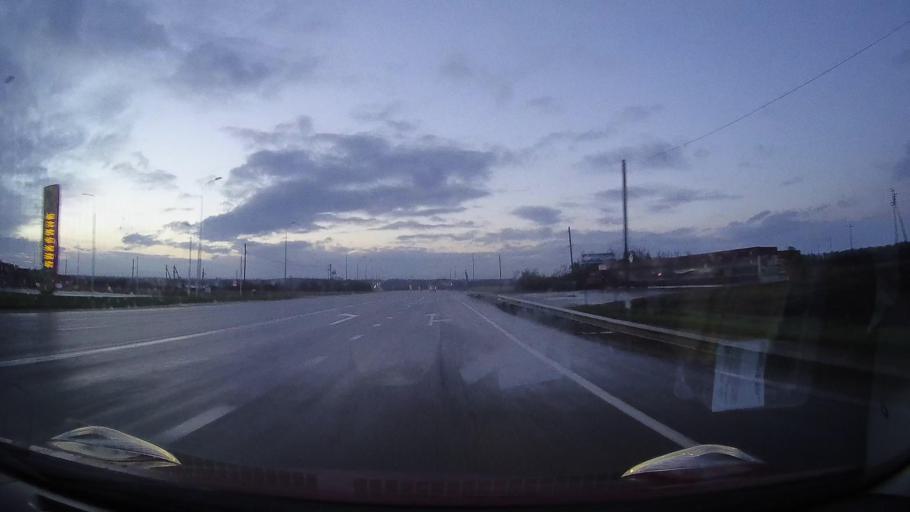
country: RU
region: Krasnodarskiy
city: Zavetnyy
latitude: 44.9097
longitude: 41.1655
